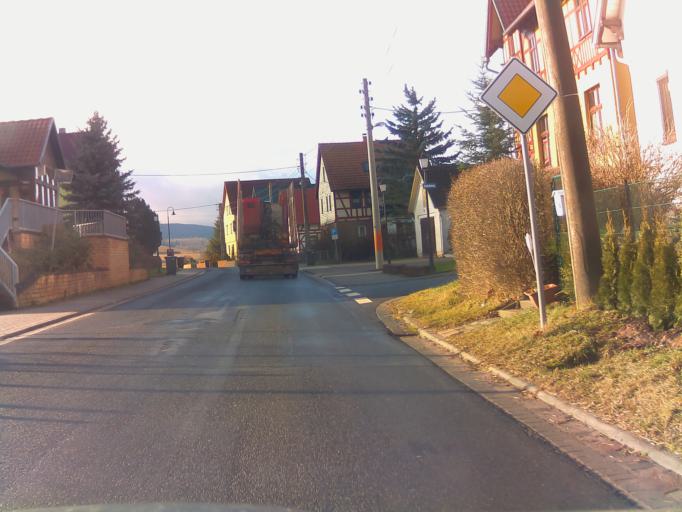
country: DE
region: Thuringia
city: Rosa
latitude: 50.7105
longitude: 10.2488
